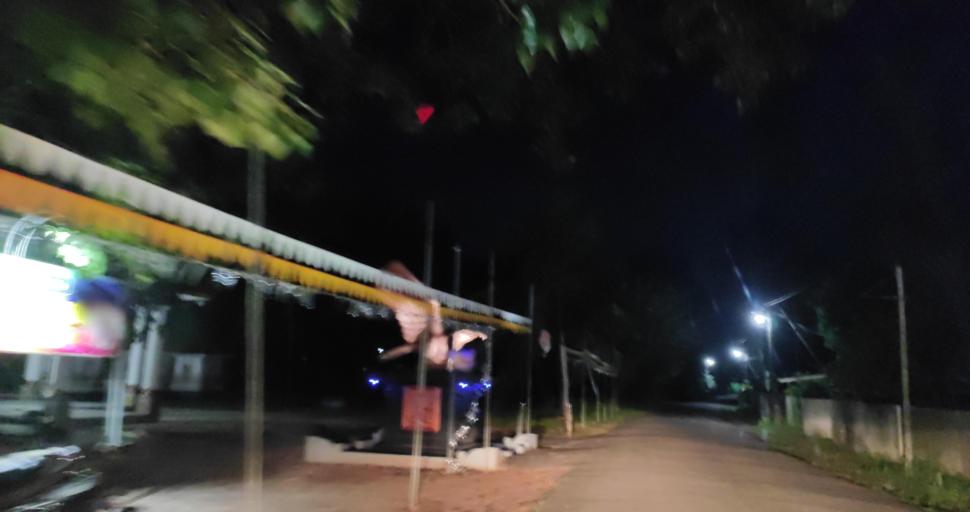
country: IN
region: Kerala
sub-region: Alappuzha
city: Shertallai
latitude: 9.6329
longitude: 76.3427
